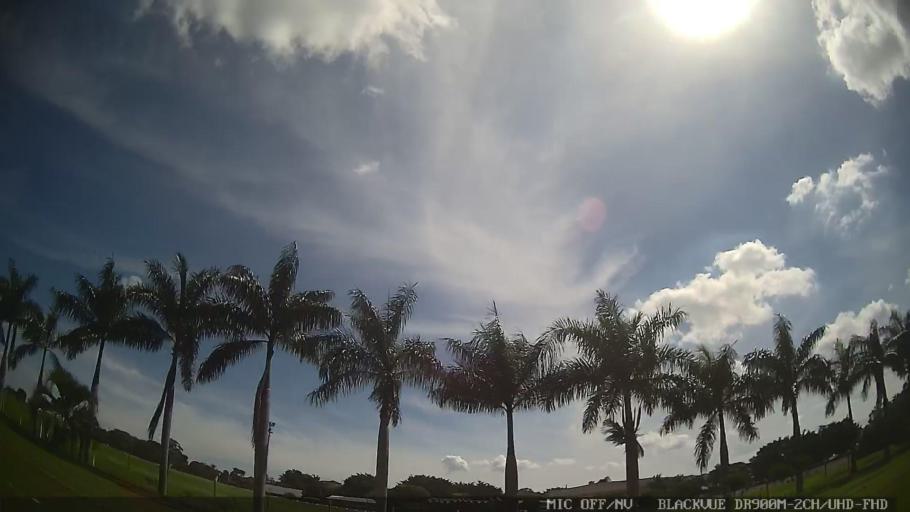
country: BR
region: Sao Paulo
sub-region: Jaguariuna
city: Jaguariuna
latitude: -22.6244
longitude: -47.0555
